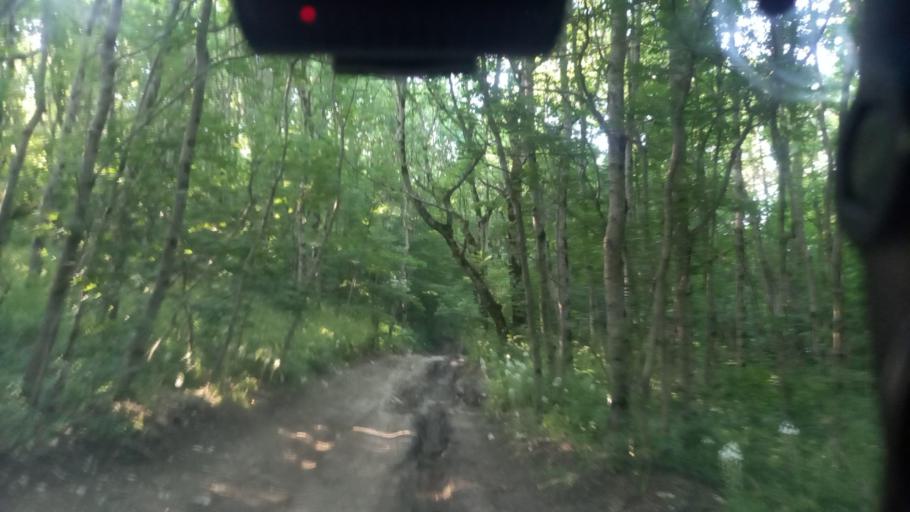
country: RU
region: Krasnodarskiy
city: Gelendzhik
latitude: 44.6194
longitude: 38.1886
